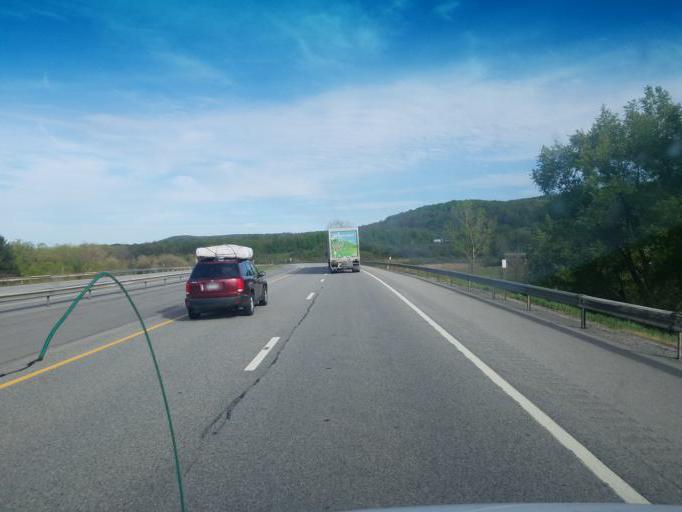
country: US
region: New York
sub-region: Herkimer County
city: Herkimer
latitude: 43.0153
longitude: -74.9784
